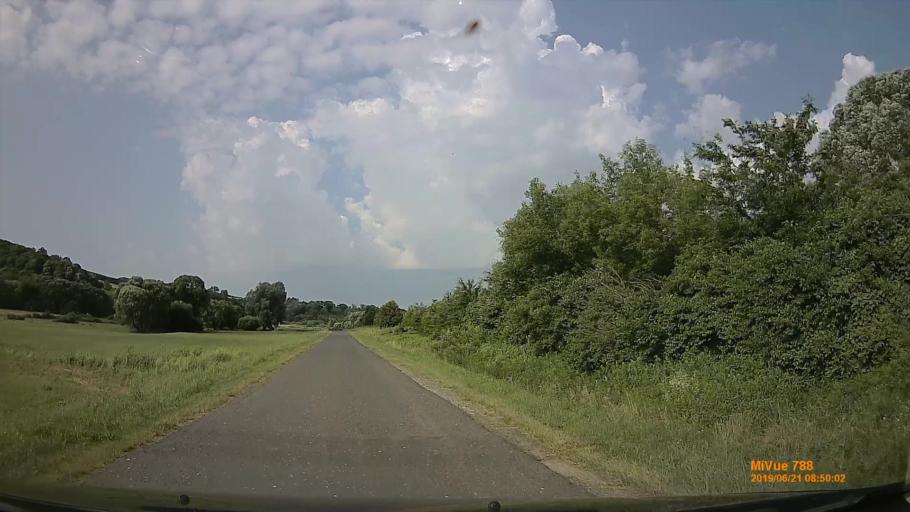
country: HU
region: Baranya
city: Buekkoesd
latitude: 46.1797
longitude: 17.9168
